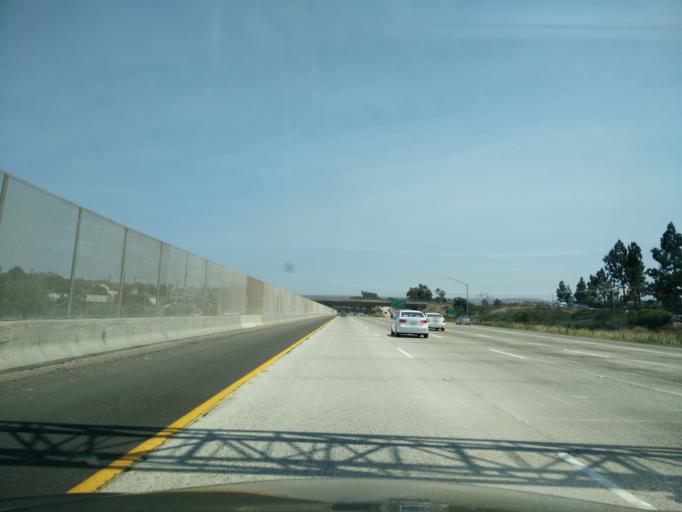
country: US
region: California
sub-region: San Diego County
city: Imperial Beach
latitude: 32.5709
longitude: -117.0781
